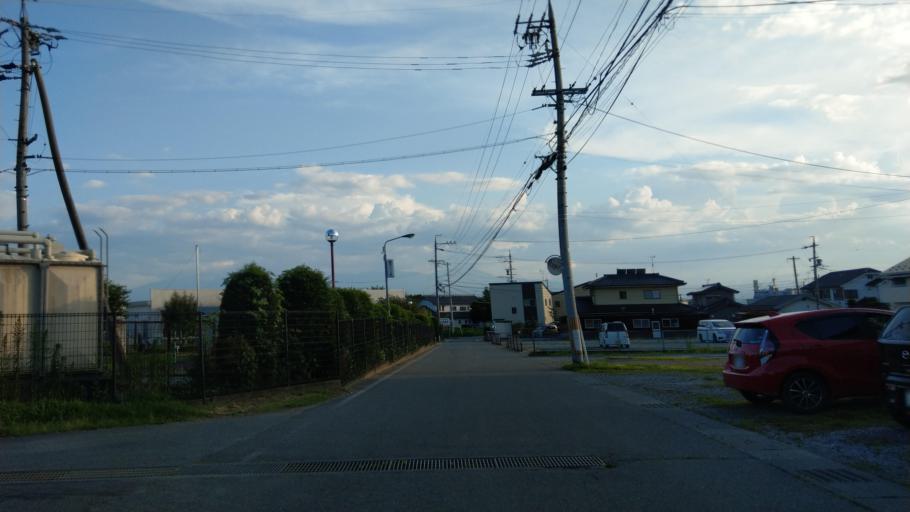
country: JP
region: Nagano
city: Komoro
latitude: 36.2894
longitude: 138.4689
